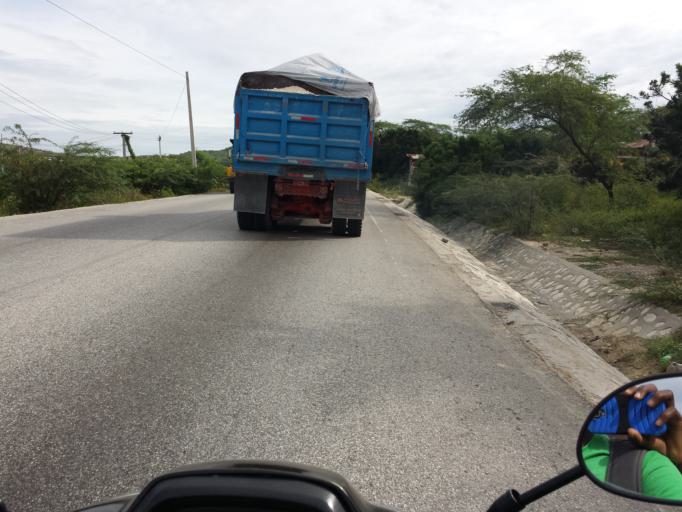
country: HT
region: Artibonite
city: Saint-Marc
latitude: 19.1367
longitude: -72.6734
